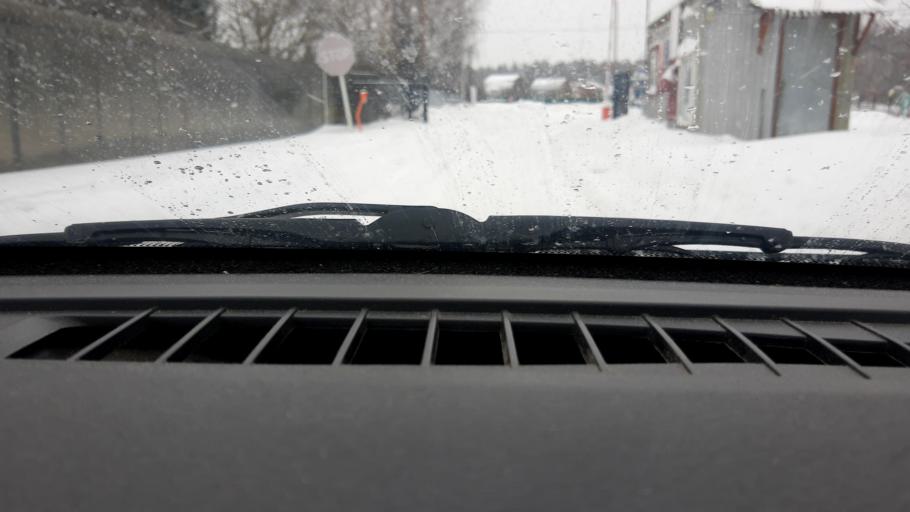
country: RU
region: Moskovskaya
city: Pirogovskiy
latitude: 56.0173
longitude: 37.7256
